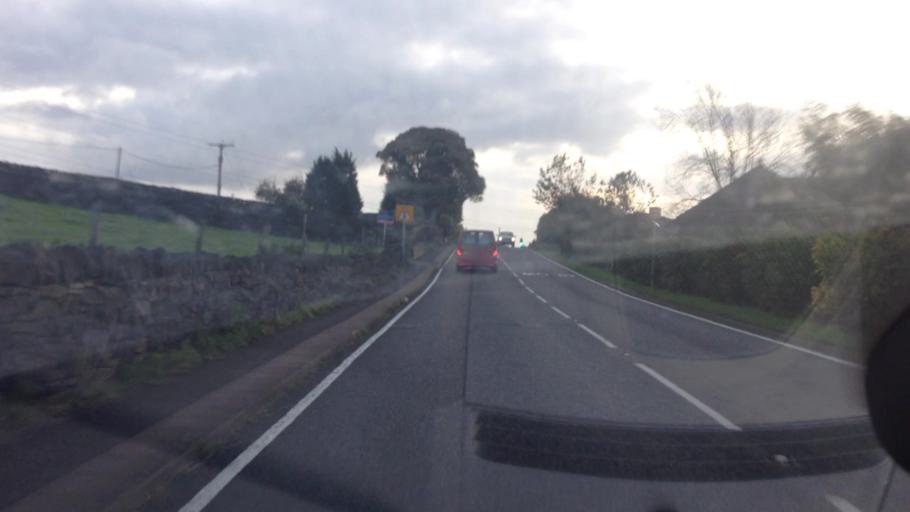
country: GB
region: England
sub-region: Kirklees
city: Mirfield
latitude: 53.6641
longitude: -1.7236
